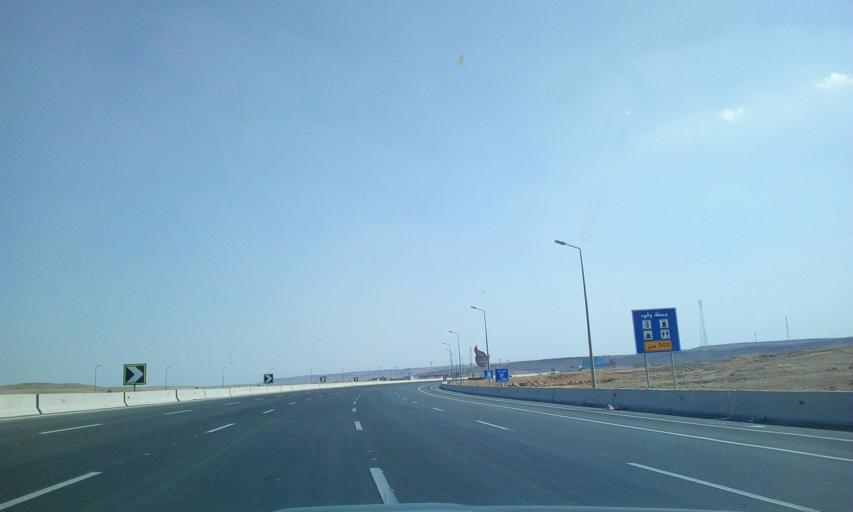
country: EG
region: As Suways
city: Ain Sukhna
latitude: 29.8120
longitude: 31.8959
